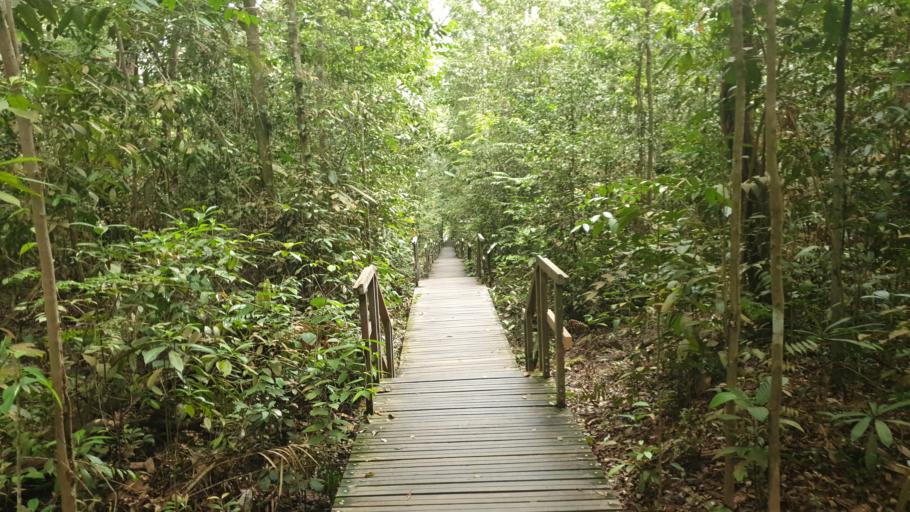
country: SG
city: Singapore
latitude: 1.3563
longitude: 103.8072
